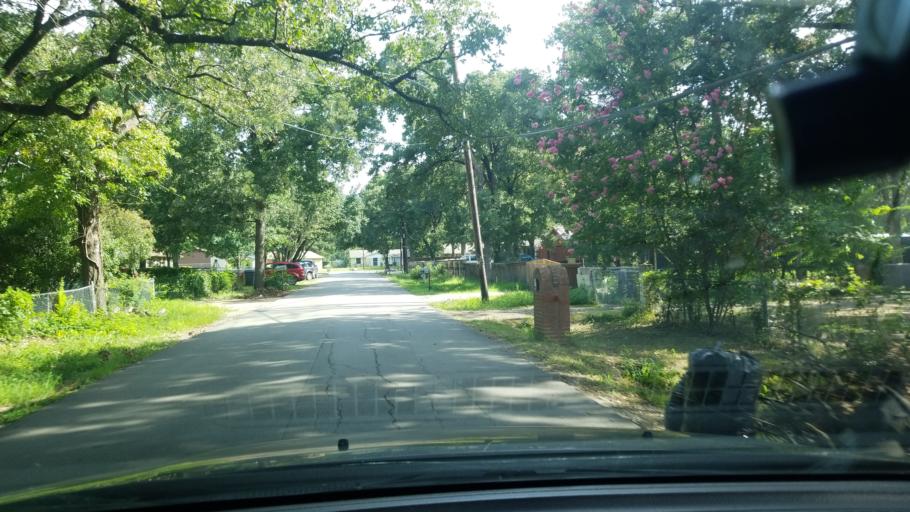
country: US
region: Texas
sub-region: Dallas County
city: Balch Springs
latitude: 32.7229
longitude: -96.6455
